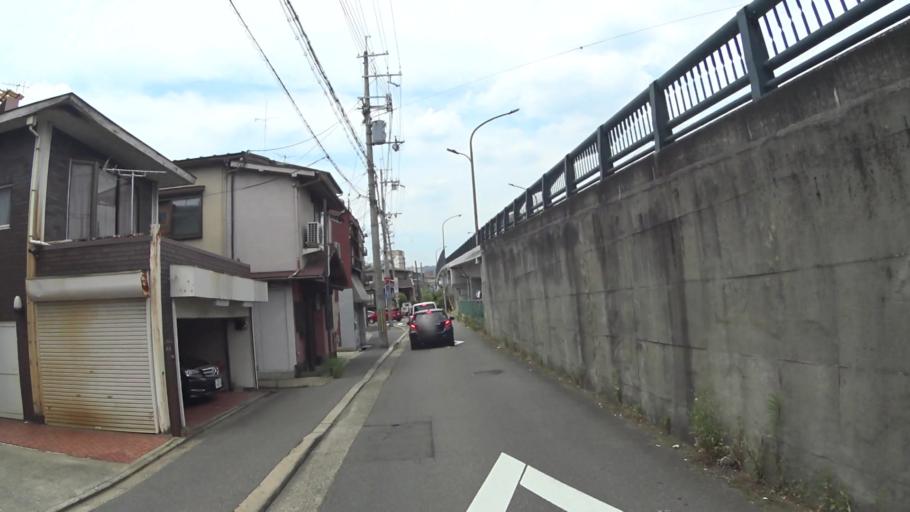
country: JP
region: Kyoto
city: Kyoto
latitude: 35.0172
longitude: 135.7147
